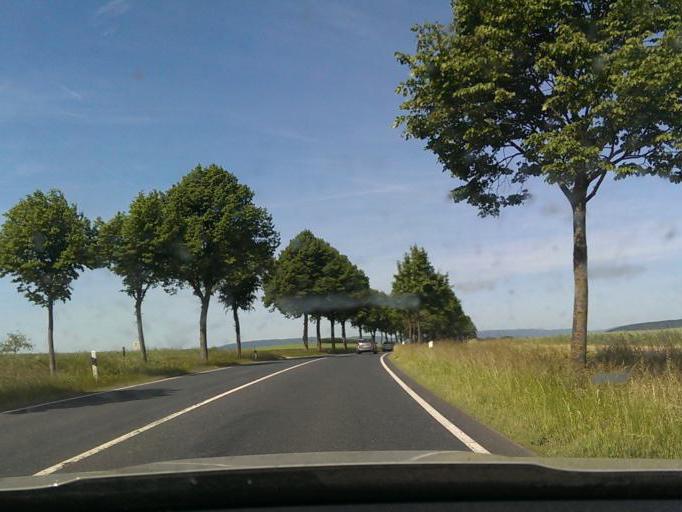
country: DE
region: Lower Saxony
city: Heyersum
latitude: 52.1568
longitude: 9.8314
